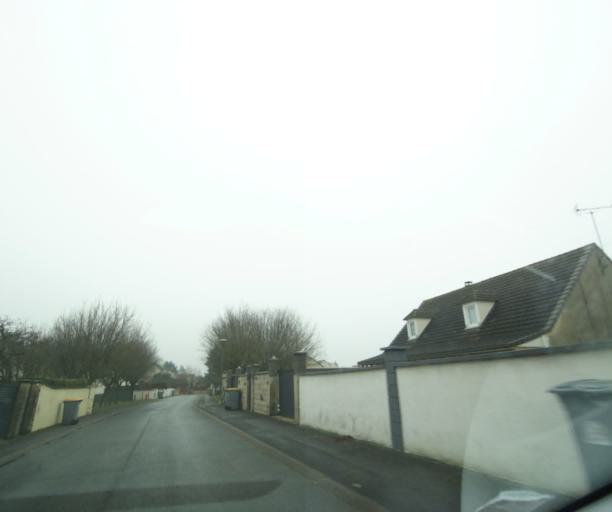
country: FR
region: Ile-de-France
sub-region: Departement de Seine-et-Marne
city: Dammartin-en-Goele
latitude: 49.0651
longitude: 2.6857
